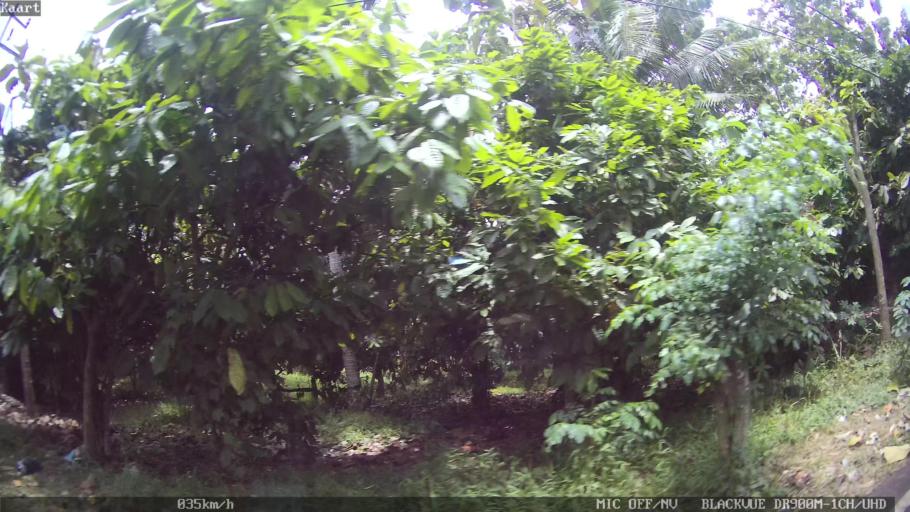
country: ID
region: Lampung
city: Bandarlampung
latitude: -5.4153
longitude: 105.2337
